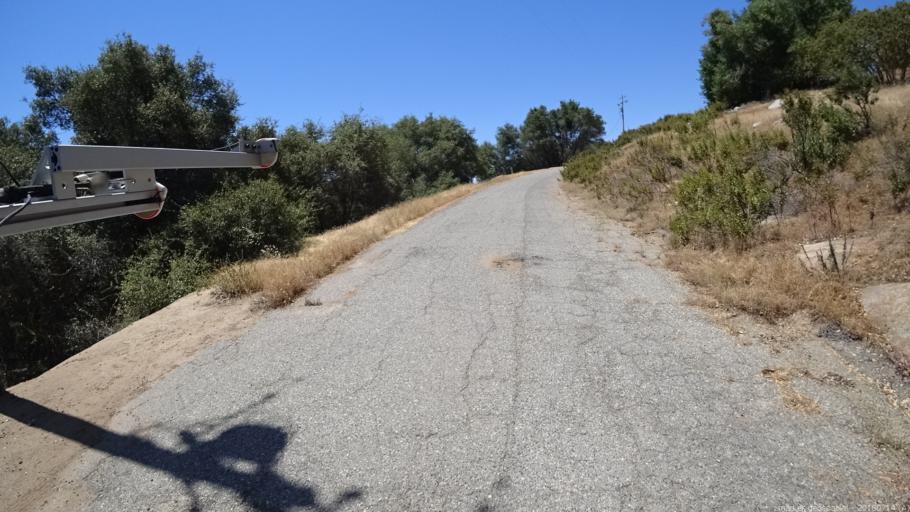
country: US
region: California
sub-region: Madera County
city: Ahwahnee
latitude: 37.3915
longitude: -119.7112
